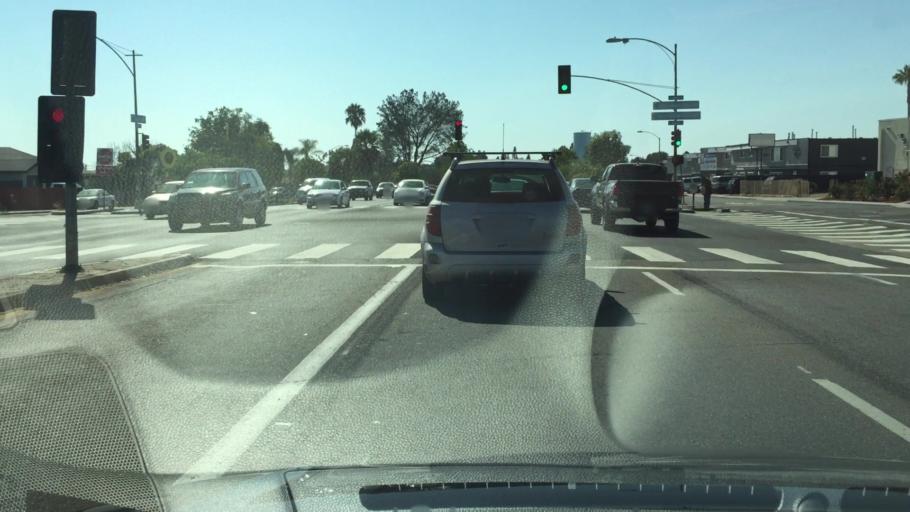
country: US
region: California
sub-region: San Diego County
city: Lemon Grove
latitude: 32.7457
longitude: -117.0585
